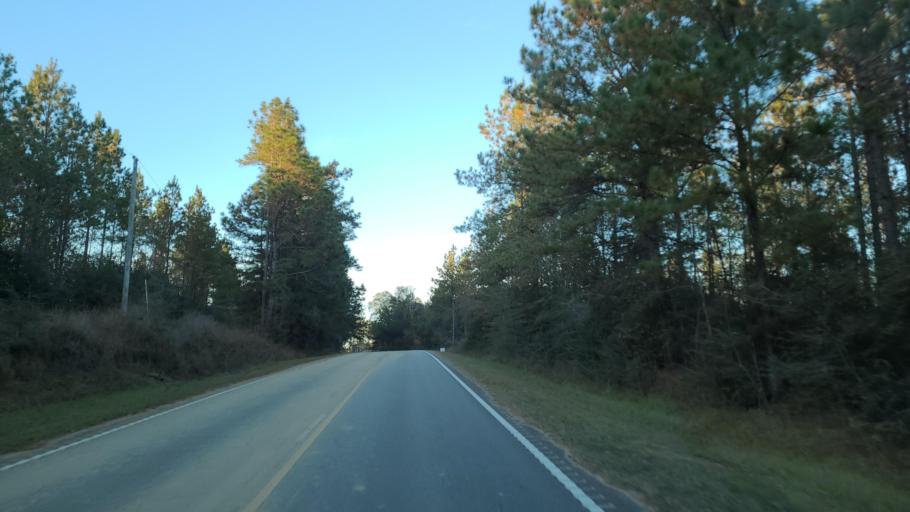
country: US
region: Mississippi
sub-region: Stone County
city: Wiggins
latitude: 31.0037
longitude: -89.2578
